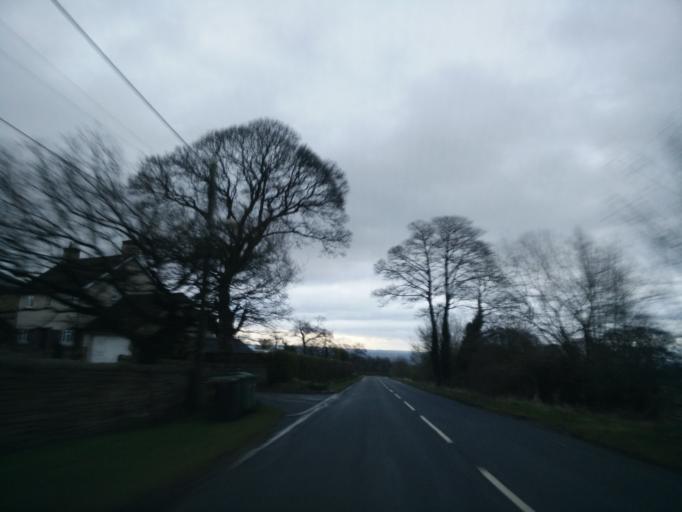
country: GB
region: England
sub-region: County Durham
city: Ushaw Moor
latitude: 54.7312
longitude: -1.6731
